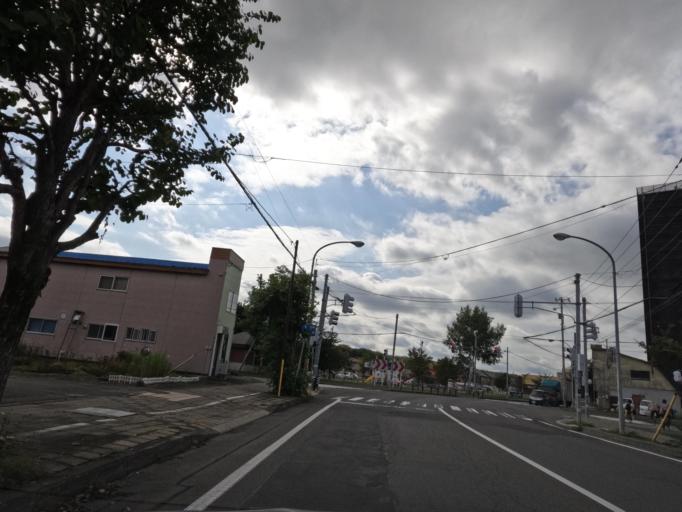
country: JP
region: Hokkaido
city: Chitose
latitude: 42.8220
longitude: 141.6425
